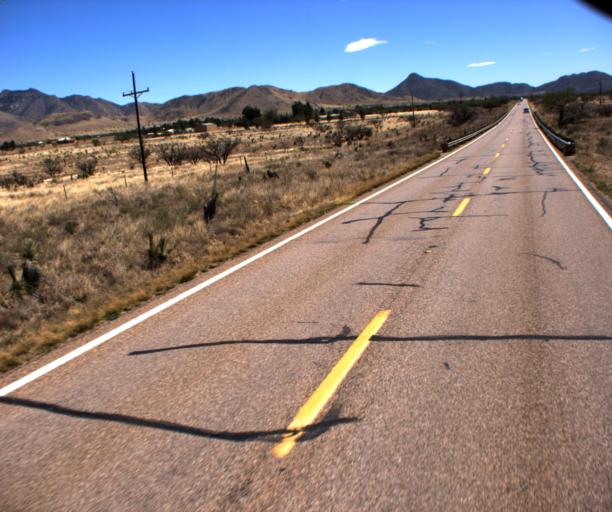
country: US
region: Arizona
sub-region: Cochise County
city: Huachuca City
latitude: 31.7240
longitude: -110.4982
